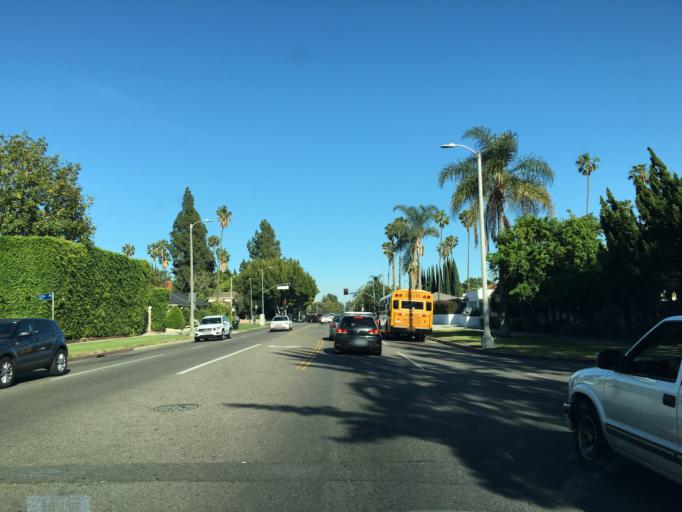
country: US
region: California
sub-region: Los Angeles County
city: Hollywood
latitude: 34.0762
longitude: -118.3399
